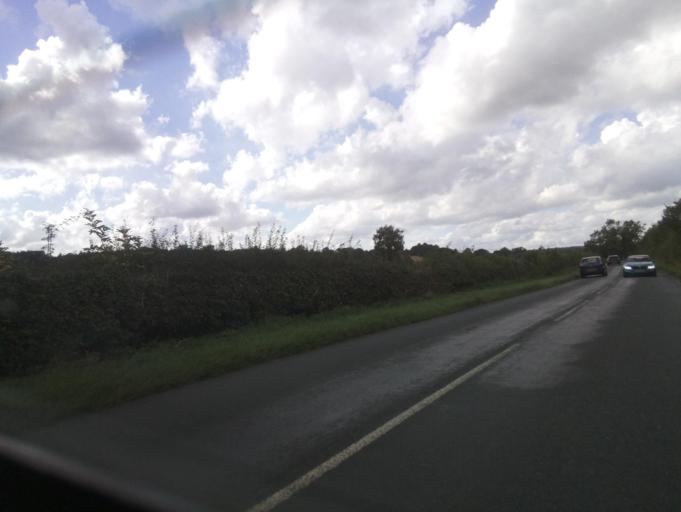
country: GB
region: England
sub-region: North Yorkshire
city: Bedale
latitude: 54.2420
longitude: -1.6864
